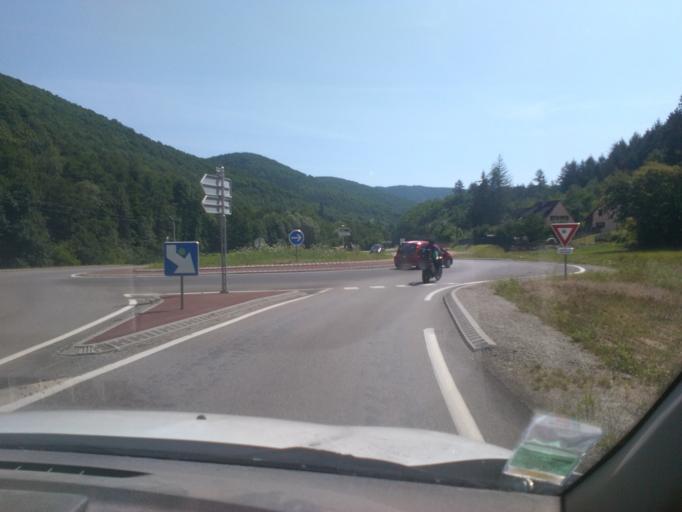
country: FR
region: Alsace
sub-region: Departement du Haut-Rhin
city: Freland
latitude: 48.1562
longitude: 7.2171
